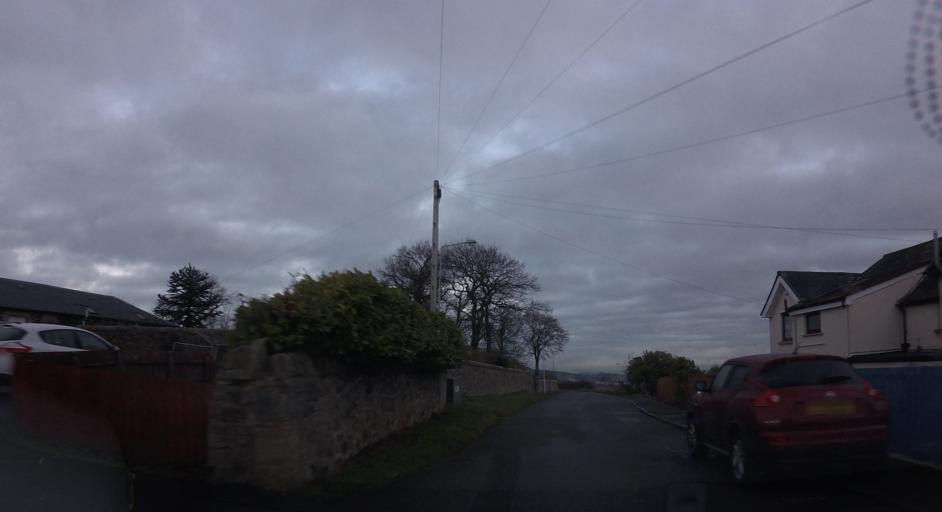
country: GB
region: Scotland
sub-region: Fife
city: Inverkeithing
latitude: 56.0288
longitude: -3.4137
